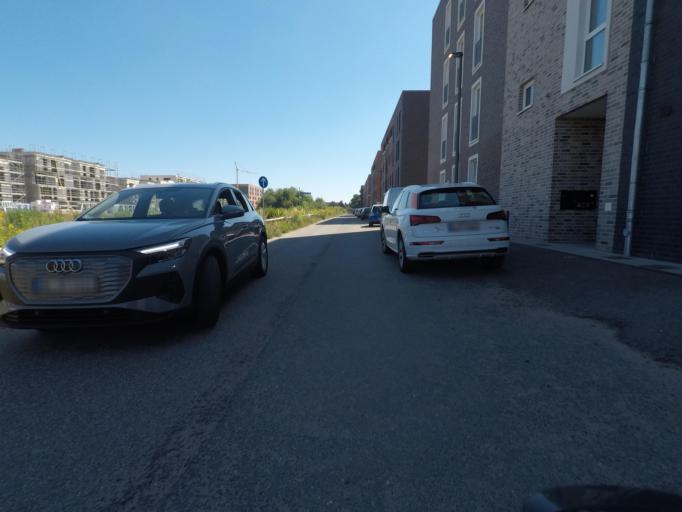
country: DE
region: Hamburg
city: Farmsen-Berne
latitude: 53.5807
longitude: 10.1337
